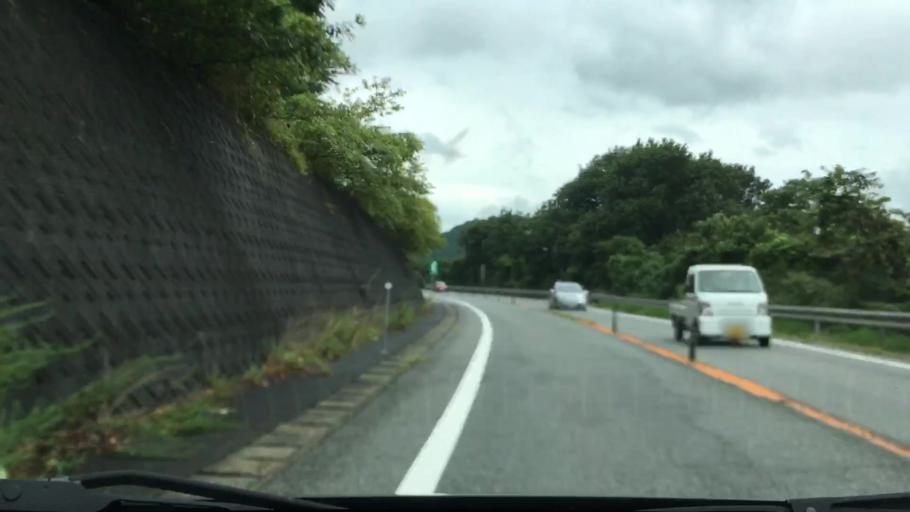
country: JP
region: Hyogo
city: Nishiwaki
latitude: 35.0319
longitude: 134.7663
